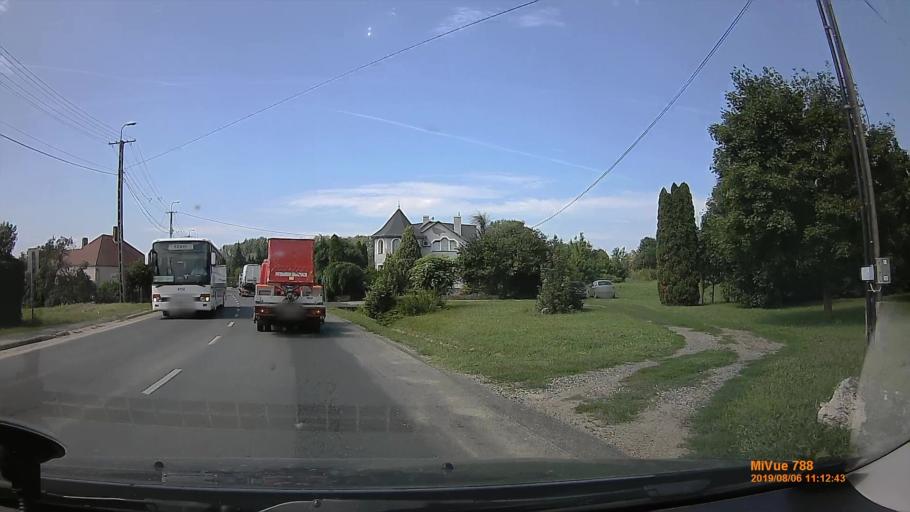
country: HU
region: Zala
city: Becsehely
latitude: 46.4456
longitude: 16.7691
